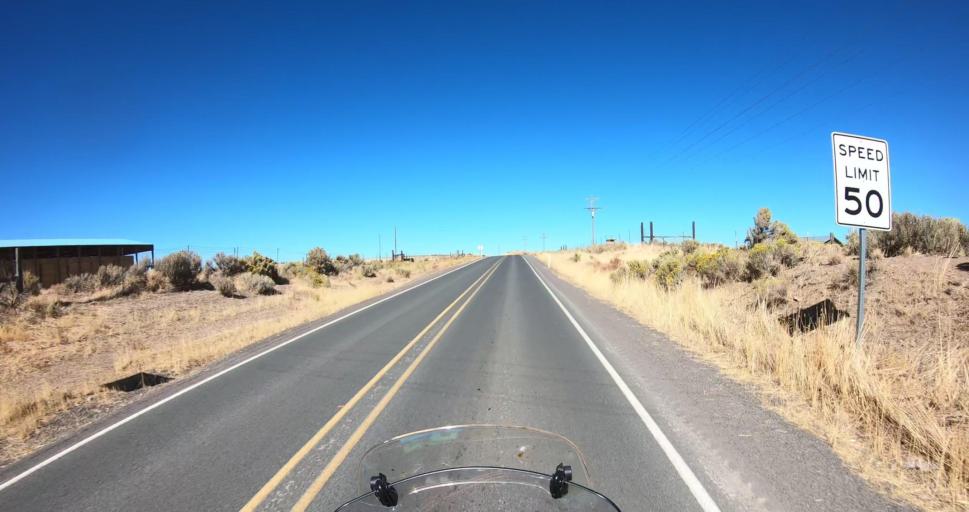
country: US
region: Oregon
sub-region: Lake County
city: Lakeview
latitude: 42.6987
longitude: -120.5463
